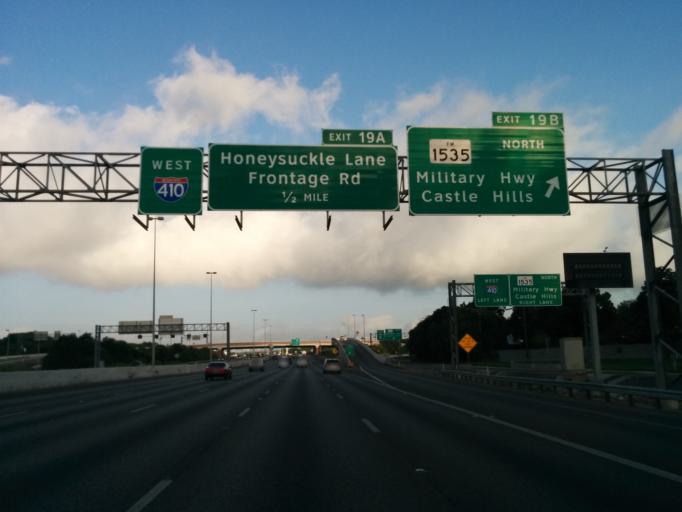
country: US
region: Texas
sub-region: Bexar County
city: Castle Hills
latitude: 29.5208
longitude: -98.5085
